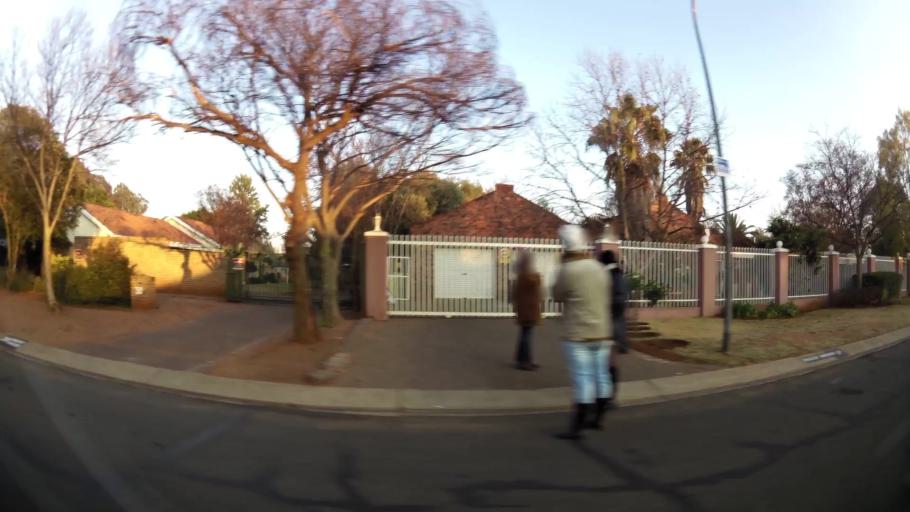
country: ZA
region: Orange Free State
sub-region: Mangaung Metropolitan Municipality
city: Bloemfontein
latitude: -29.1034
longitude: 26.1495
